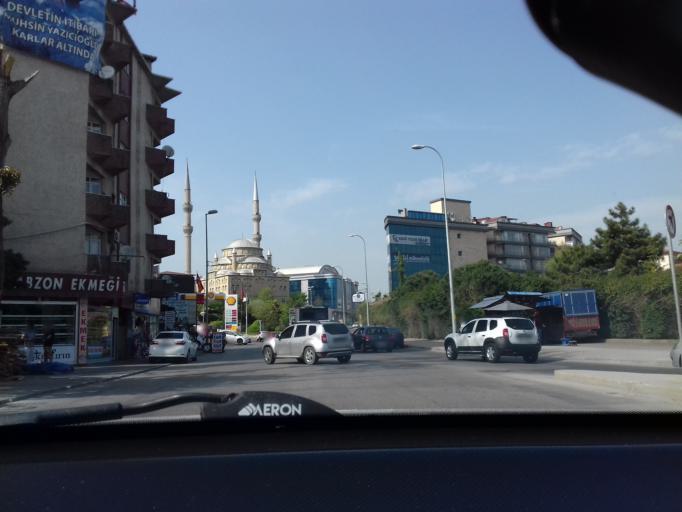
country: TR
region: Istanbul
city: Samandira
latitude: 40.9798
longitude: 29.2205
